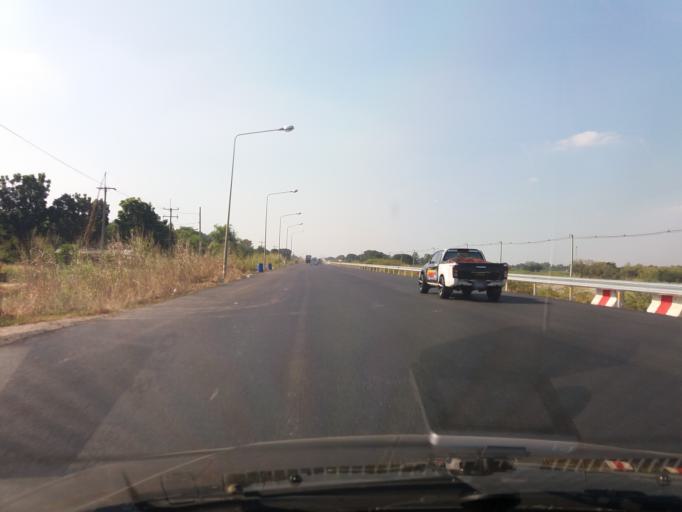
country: TH
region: Nakhon Sawan
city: Krok Phra
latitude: 15.6250
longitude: 100.1106
